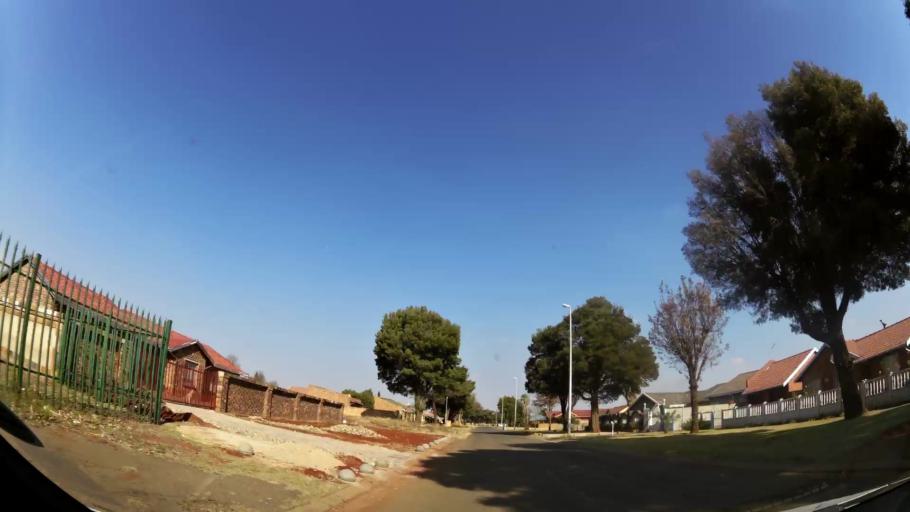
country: ZA
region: Gauteng
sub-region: Ekurhuleni Metropolitan Municipality
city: Brakpan
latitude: -26.2326
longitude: 28.3335
